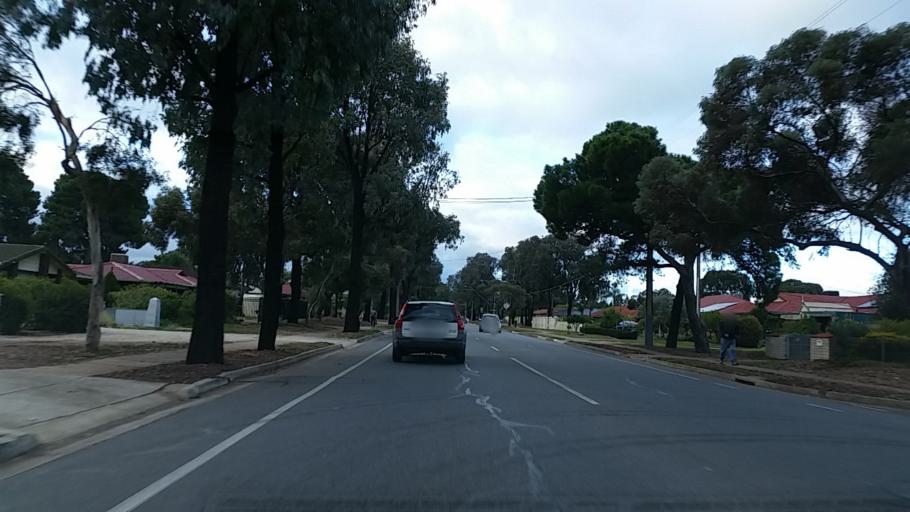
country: AU
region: South Australia
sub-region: Salisbury
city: Salisbury
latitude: -34.7632
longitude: 138.6565
